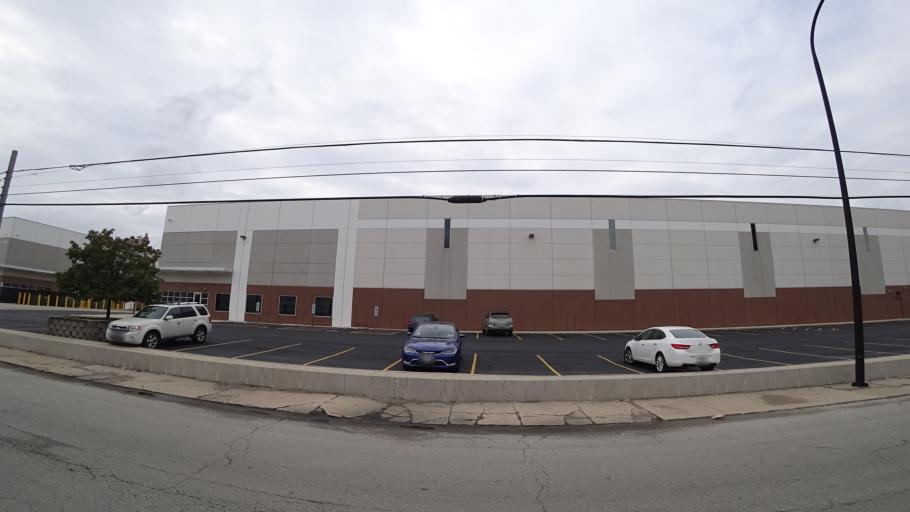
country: US
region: Illinois
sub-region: Cook County
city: Cicero
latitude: 41.8617
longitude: -87.7593
